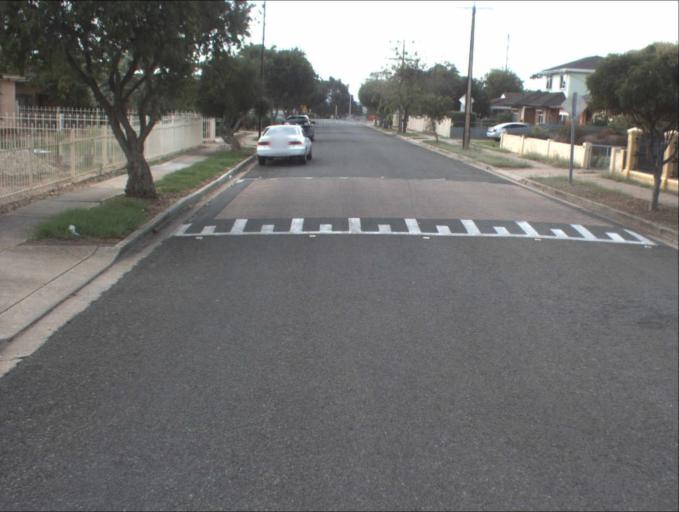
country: AU
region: South Australia
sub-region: Salisbury
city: Ingle Farm
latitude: -34.8490
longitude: 138.6225
